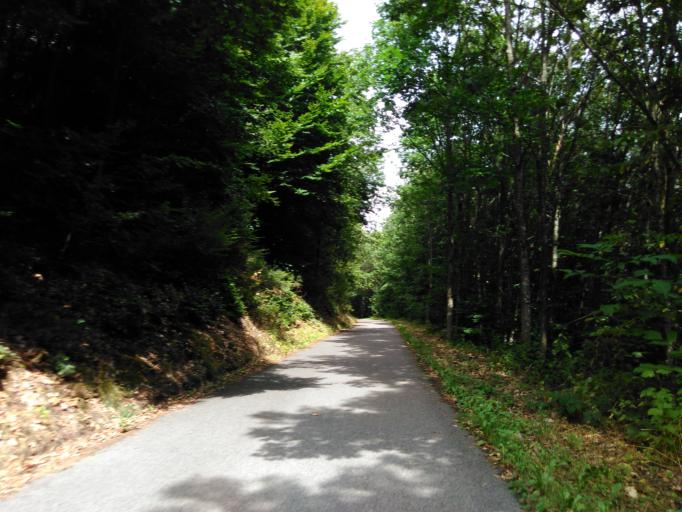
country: LU
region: Grevenmacher
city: Gonderange
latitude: 49.6653
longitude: 6.2265
